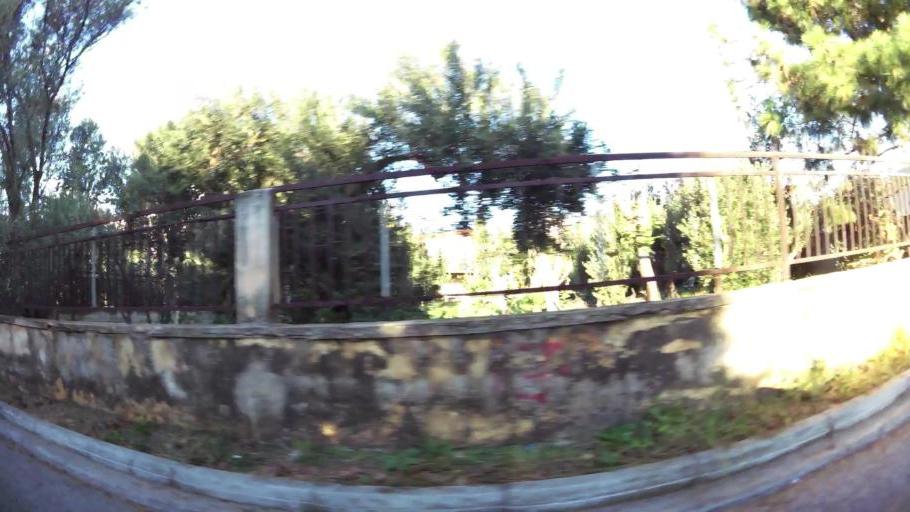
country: GR
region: Attica
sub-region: Nomarchia Athinas
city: Vrilissia
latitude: 38.0280
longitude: 23.8388
